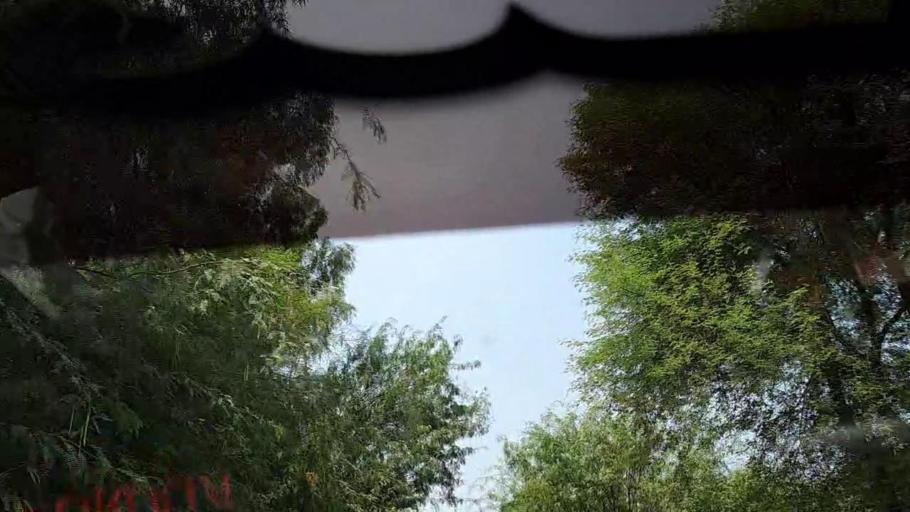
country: PK
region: Sindh
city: Pano Aqil
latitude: 27.9171
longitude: 69.2055
